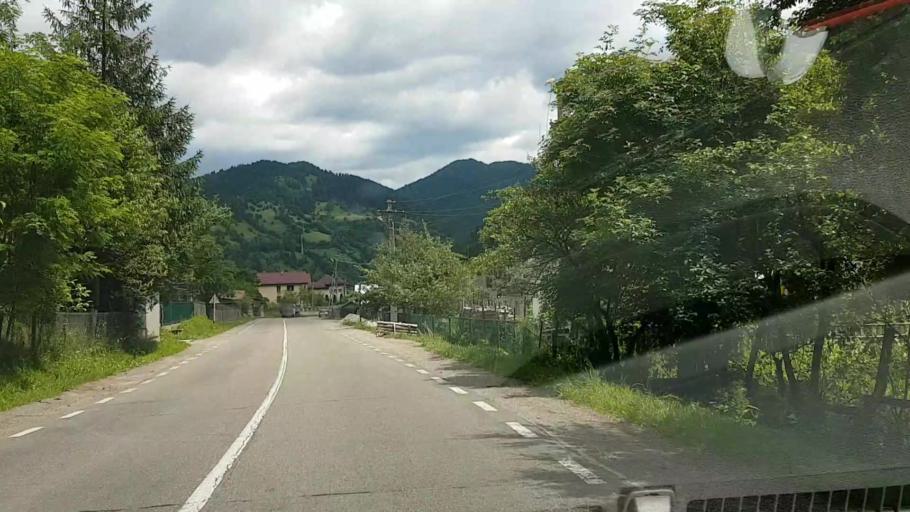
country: RO
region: Suceava
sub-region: Comuna Brosteni
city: Brosteni
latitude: 47.2167
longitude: 25.7395
